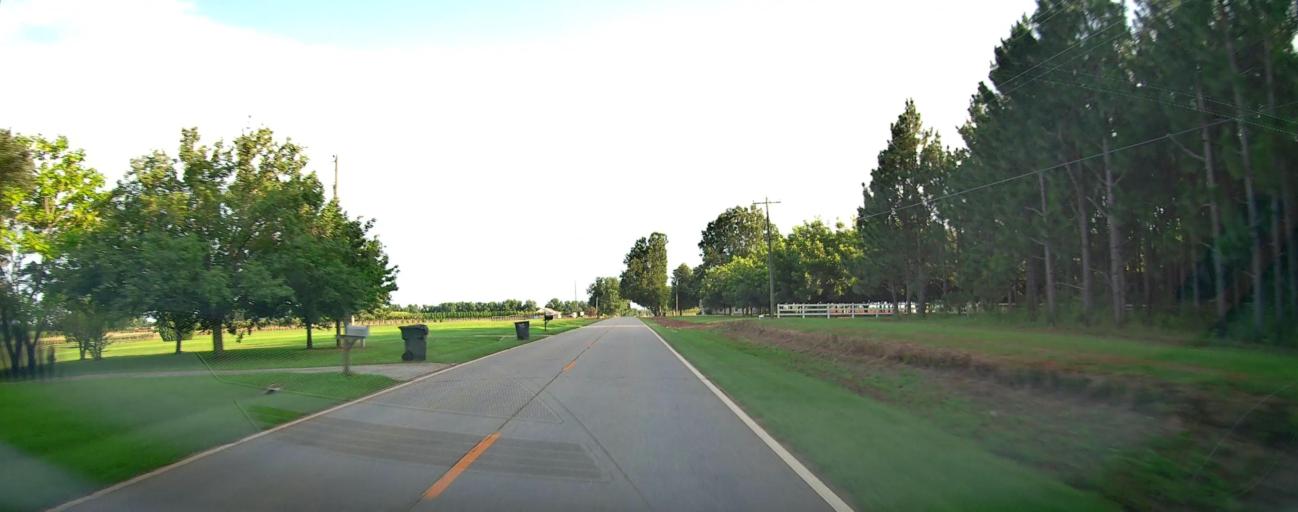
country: US
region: Georgia
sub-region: Peach County
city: Byron
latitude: 32.6642
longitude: -83.8608
